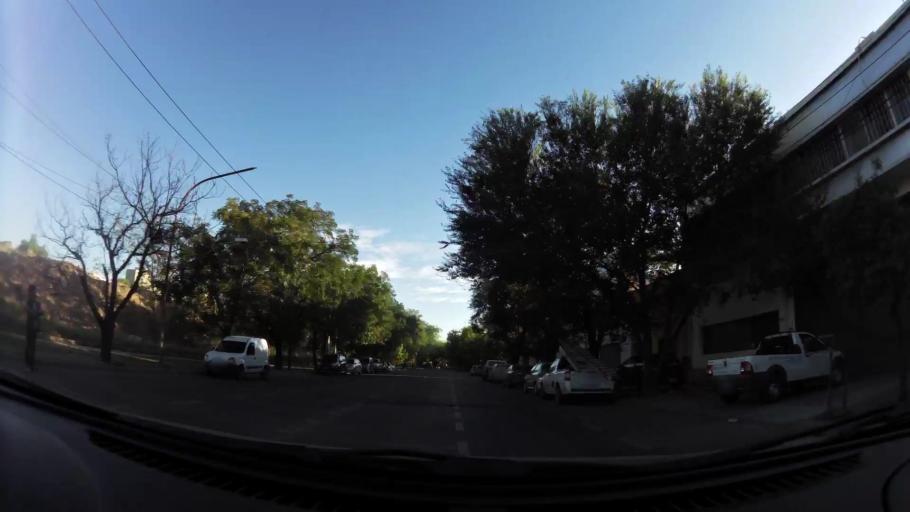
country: AR
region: Mendoza
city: Mendoza
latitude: -32.8808
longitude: -68.8462
